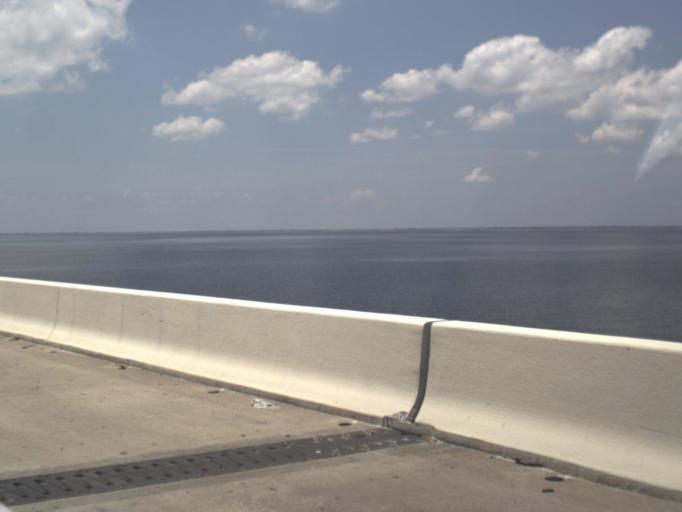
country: US
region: Florida
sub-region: Hillsborough County
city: Town 'n' Country
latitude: 27.9336
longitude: -82.5724
